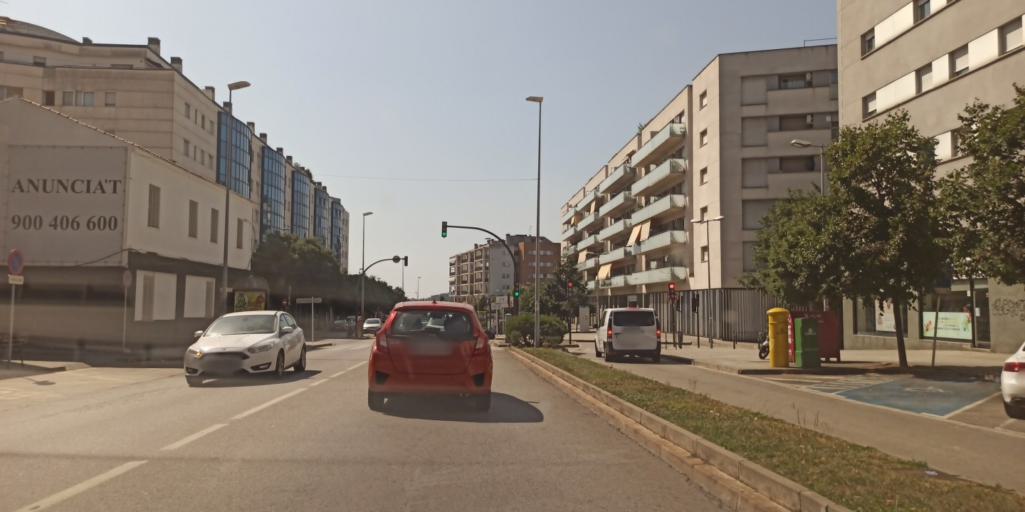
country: ES
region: Catalonia
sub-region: Provincia de Barcelona
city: Cerdanyola del Valles
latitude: 41.4983
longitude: 2.1417
